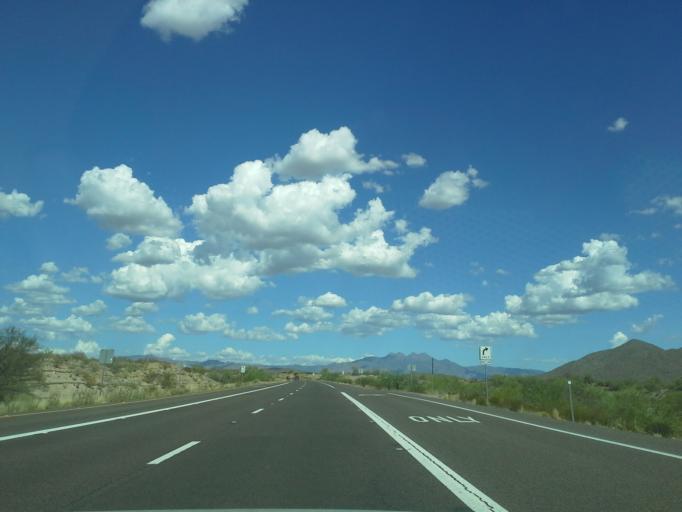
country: US
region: Arizona
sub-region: Maricopa County
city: Fountain Hills
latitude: 33.5852
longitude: -111.6062
